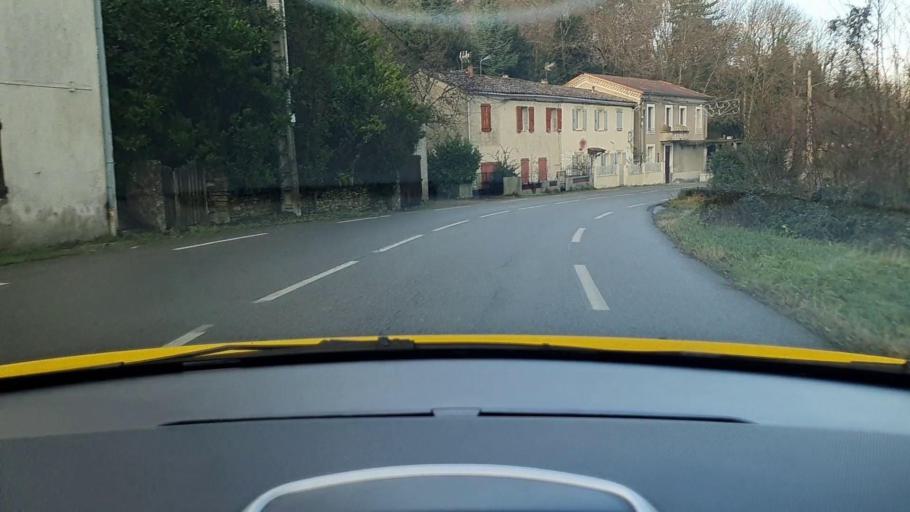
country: FR
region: Languedoc-Roussillon
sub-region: Departement du Gard
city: Branoux-les-Taillades
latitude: 44.2777
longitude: 4.0048
